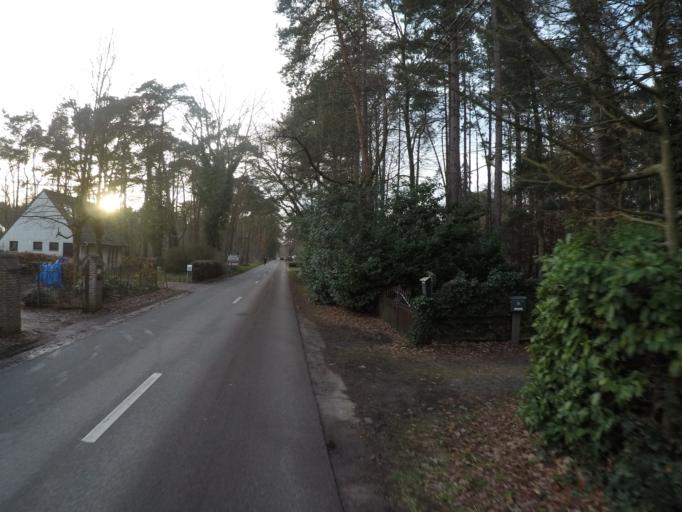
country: BE
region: Flanders
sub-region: Provincie Antwerpen
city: Brecht
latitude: 51.3226
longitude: 4.5734
